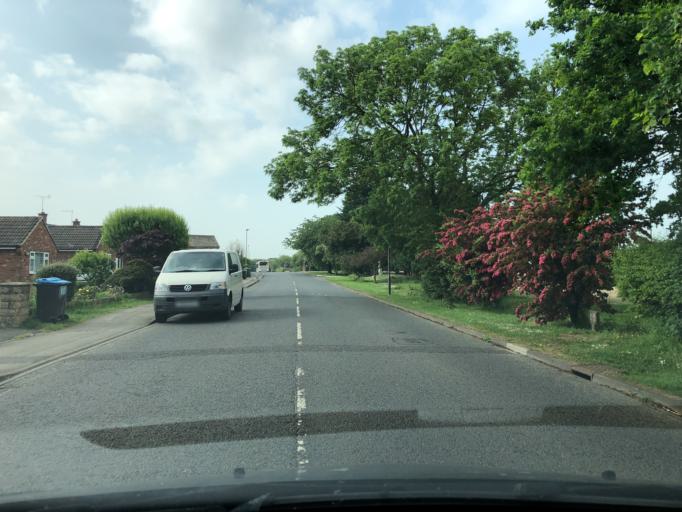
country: GB
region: England
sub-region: North Yorkshire
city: Northallerton
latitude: 54.3281
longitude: -1.4524
